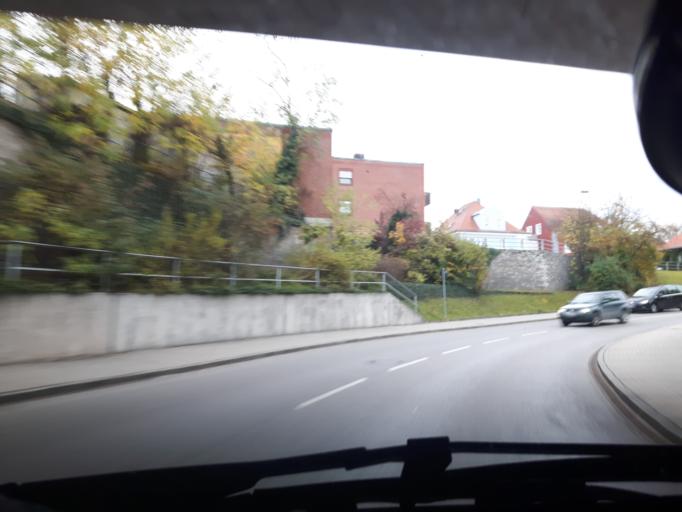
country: DE
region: Bavaria
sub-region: Regierungsbezirk Mittelfranken
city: Gunzenhausen
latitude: 49.1201
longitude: 10.7543
